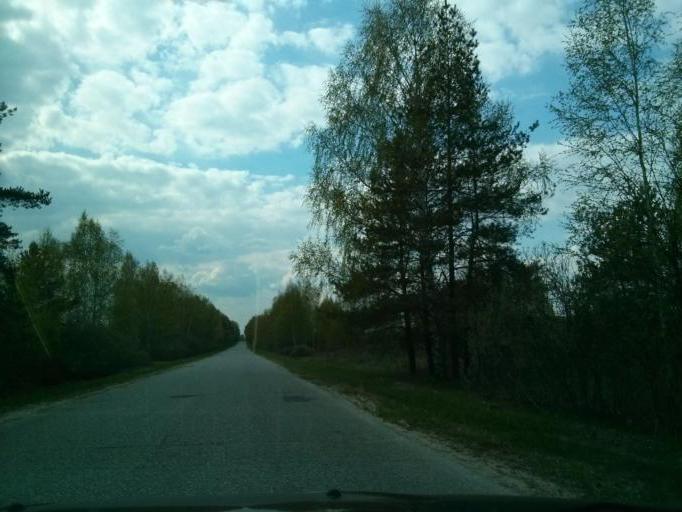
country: RU
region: Nizjnij Novgorod
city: Shimorskoye
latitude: 55.3384
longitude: 41.8859
